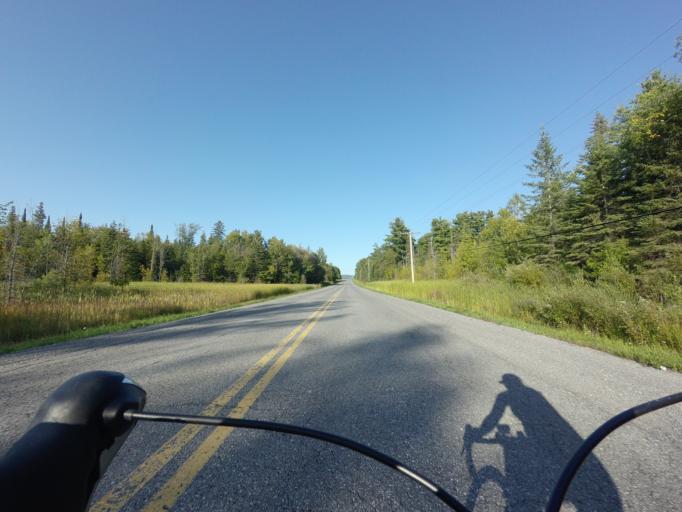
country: CA
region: Ontario
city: Bells Corners
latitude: 45.4620
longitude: -76.0150
